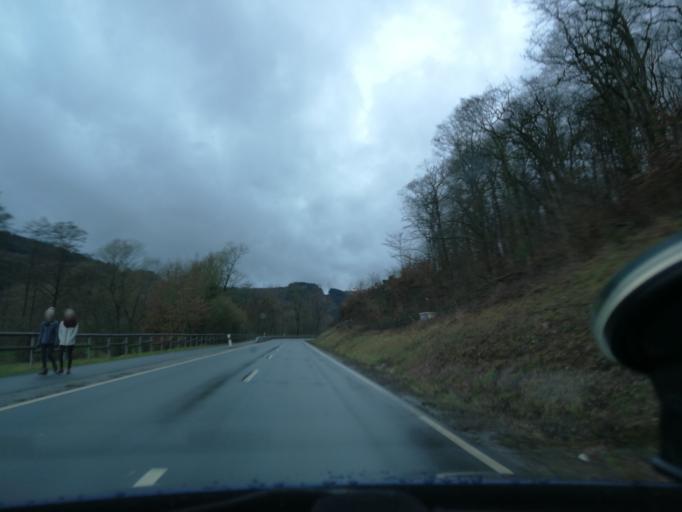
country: DE
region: Rheinland-Pfalz
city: Salmtal
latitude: 49.9295
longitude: 6.8337
